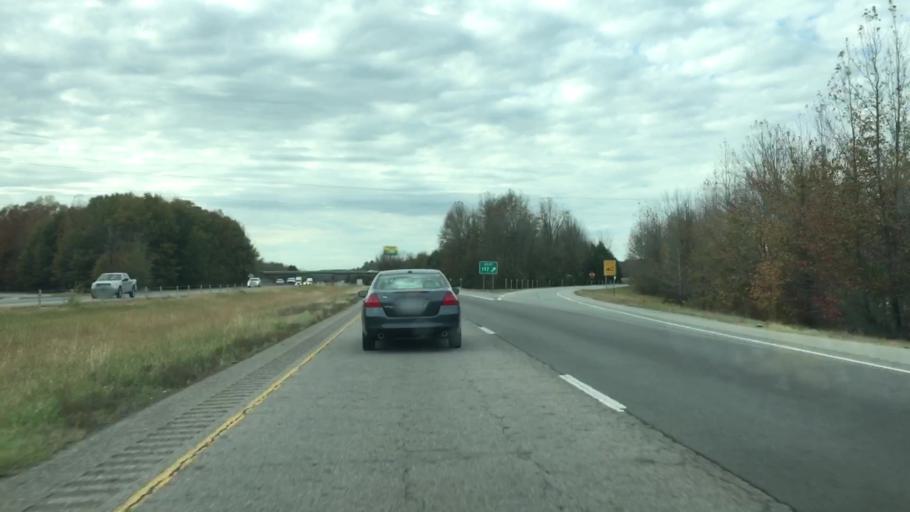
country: US
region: Arkansas
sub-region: Faulkner County
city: Conway
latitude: 35.1520
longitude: -92.5492
